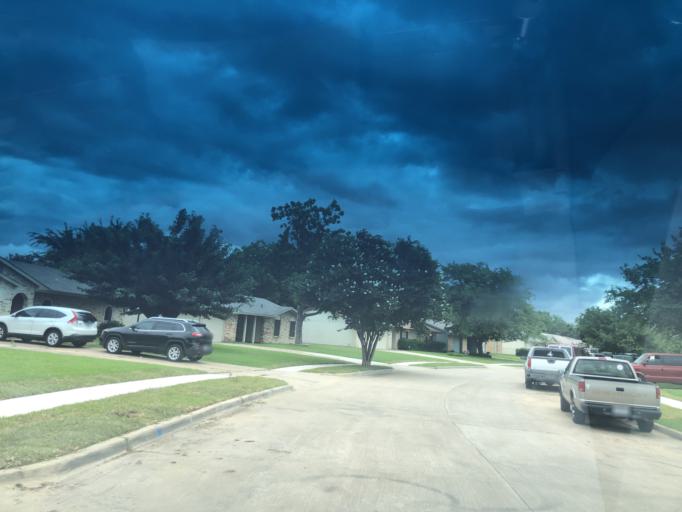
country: US
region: Texas
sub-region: Dallas County
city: Grand Prairie
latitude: 32.7066
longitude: -97.0057
